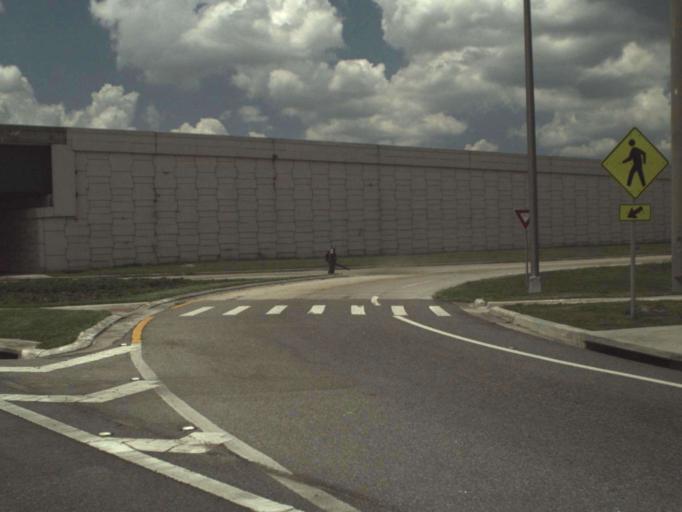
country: US
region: Florida
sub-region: Orange County
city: Lockhart
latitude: 28.6414
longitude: -81.4154
